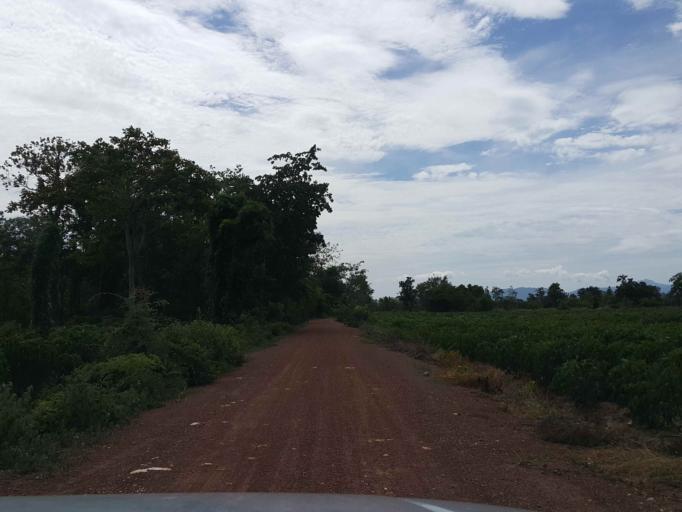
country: TH
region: Sukhothai
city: Ban Dan Lan Hoi
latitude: 17.0940
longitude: 99.4724
